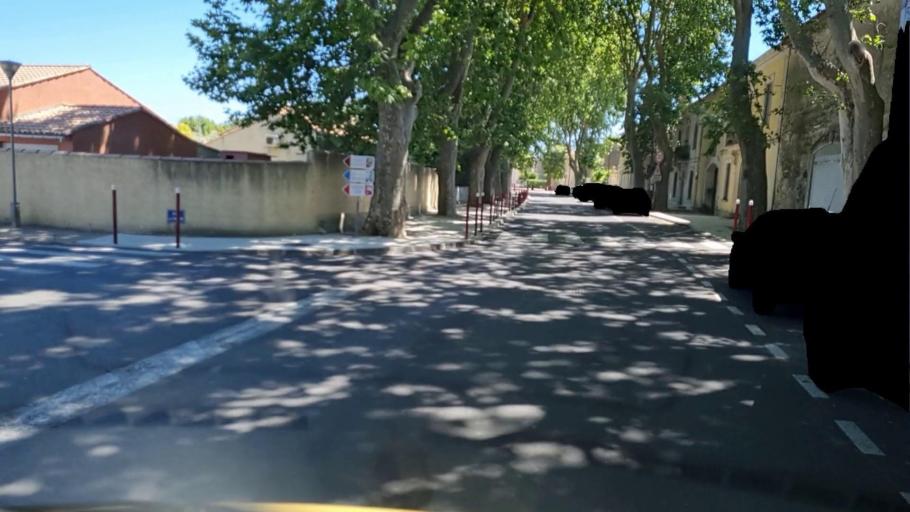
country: FR
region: Languedoc-Roussillon
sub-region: Departement du Gard
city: Le Cailar
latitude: 43.6785
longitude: 4.2354
